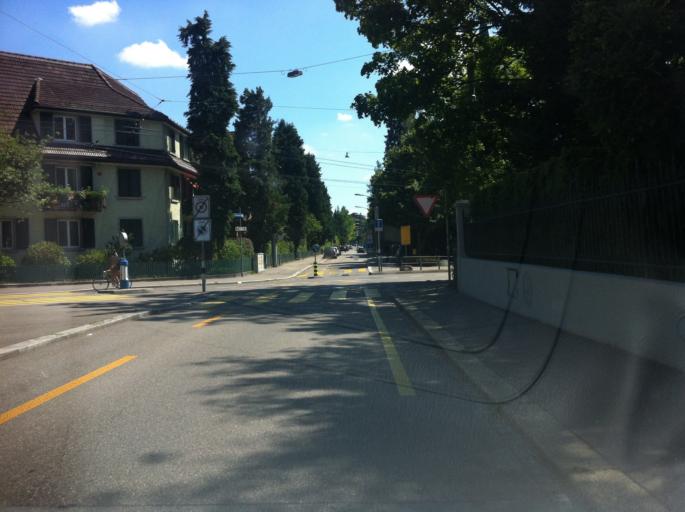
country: CH
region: Zurich
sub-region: Bezirk Zuerich
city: Zuerich (Kreis 8) / Muehlebach
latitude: 47.3591
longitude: 8.5568
